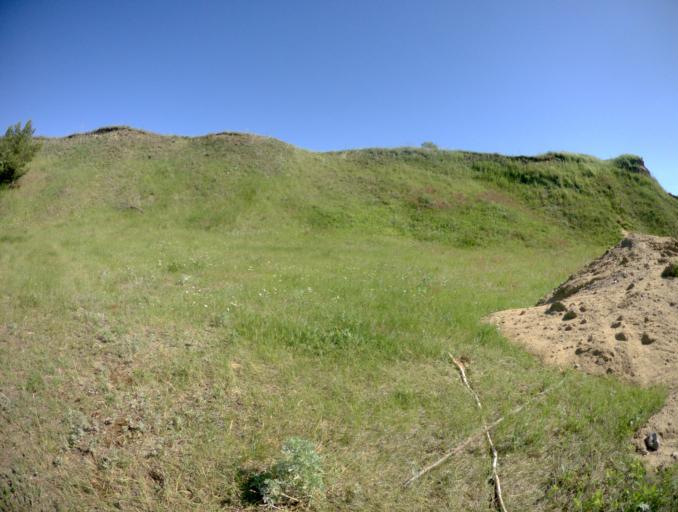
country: RU
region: Ivanovo
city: Gavrilov Posad
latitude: 56.5317
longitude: 40.2009
